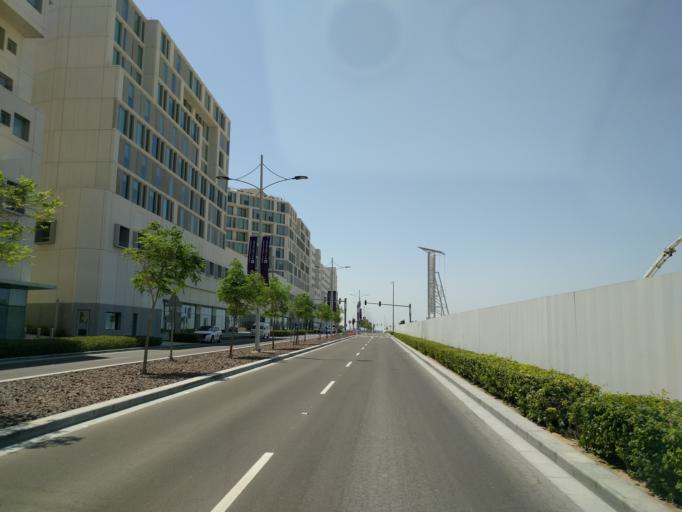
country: AE
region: Abu Dhabi
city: Abu Dhabi
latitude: 24.5241
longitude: 54.4326
